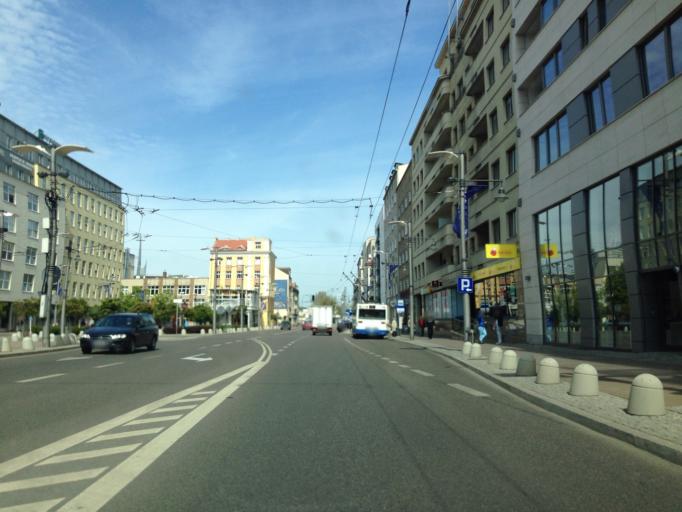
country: PL
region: Pomeranian Voivodeship
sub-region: Gdynia
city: Gdynia
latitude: 54.5220
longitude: 18.5433
